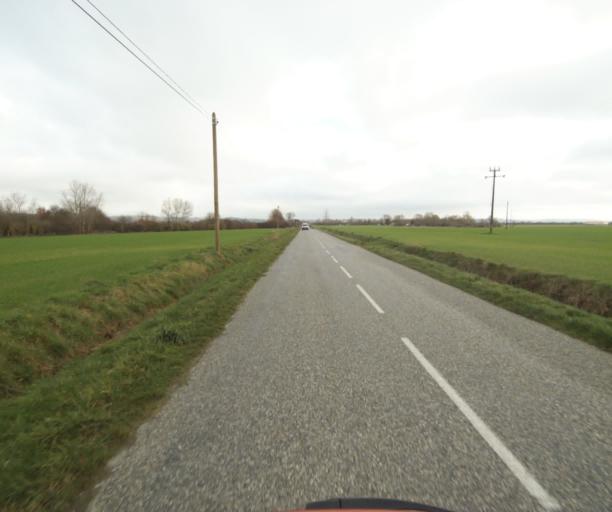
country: FR
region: Languedoc-Roussillon
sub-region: Departement de l'Aude
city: Belpech
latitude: 43.2196
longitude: 1.7110
